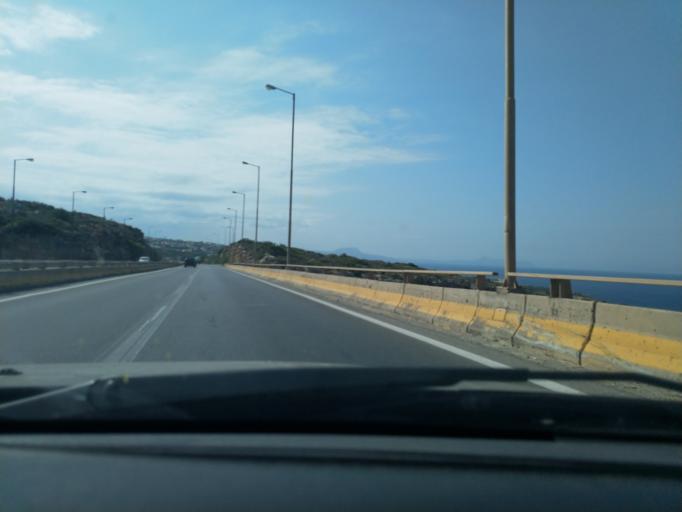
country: GR
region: Crete
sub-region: Nomos Rethymnis
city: Rethymno
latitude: 35.3583
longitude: 24.4602
